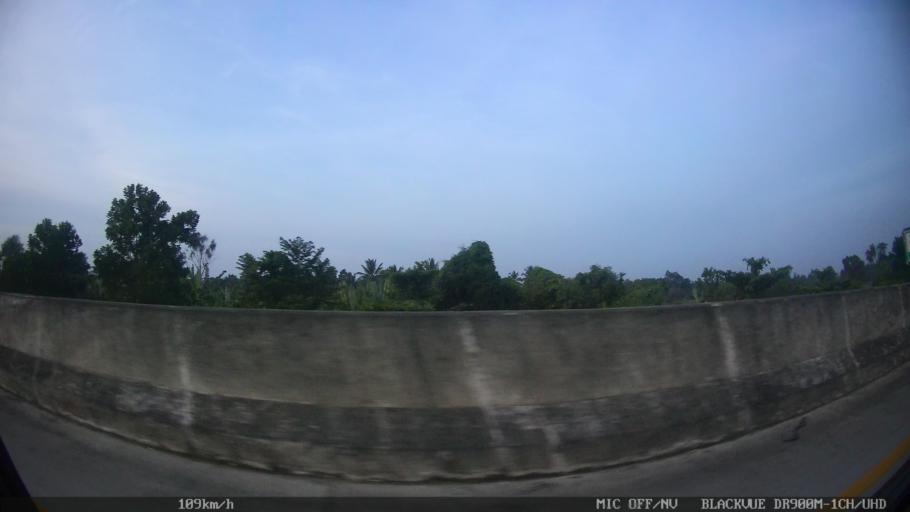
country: ID
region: Lampung
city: Pasuruan
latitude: -5.7462
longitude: 105.7012
